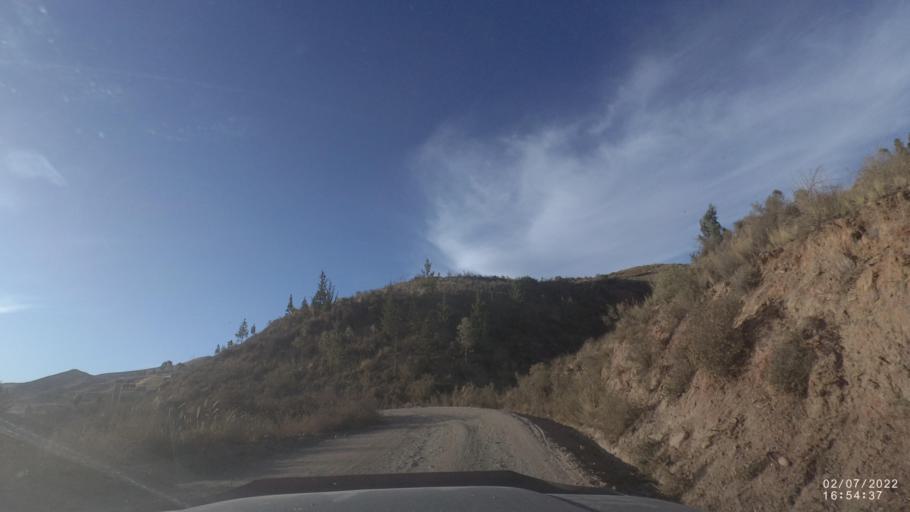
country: BO
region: Cochabamba
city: Irpa Irpa
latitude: -17.9650
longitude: -66.5396
